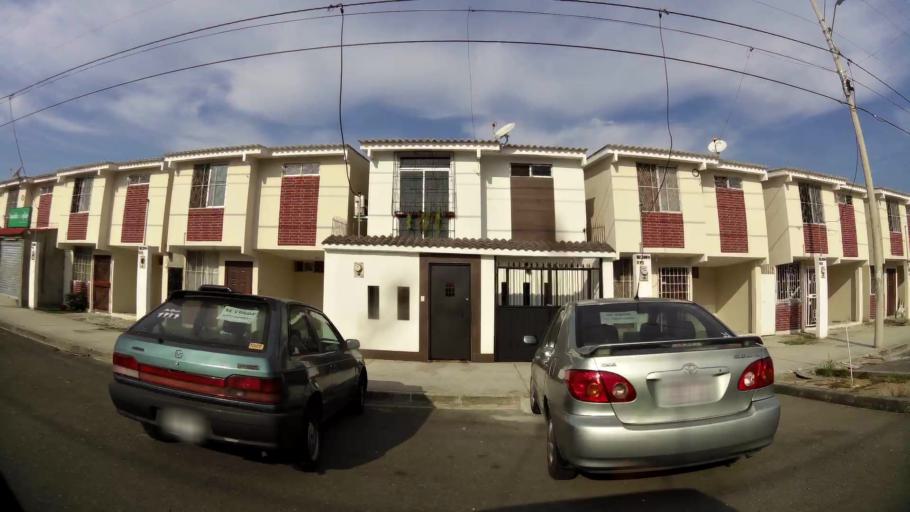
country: EC
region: Guayas
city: Eloy Alfaro
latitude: -2.0631
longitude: -79.8950
